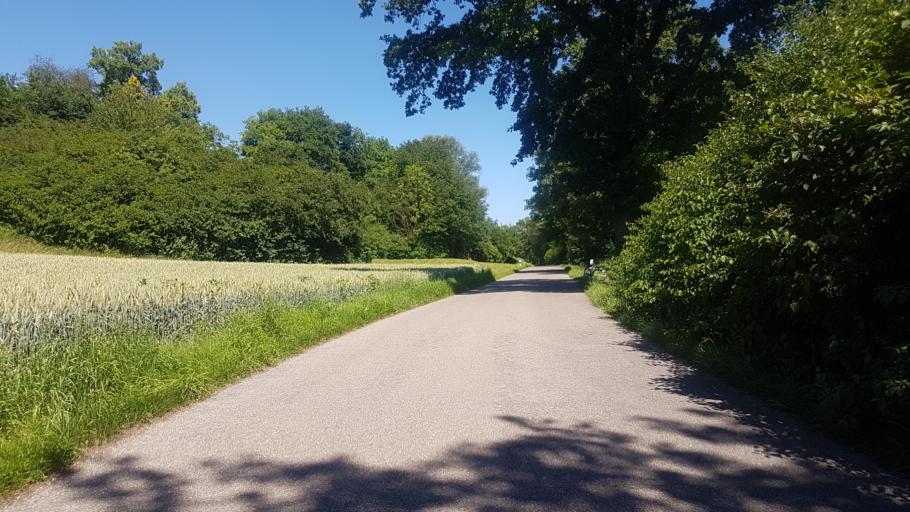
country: DE
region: Bavaria
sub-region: Upper Bavaria
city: Vohburg an der Donau
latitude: 48.7834
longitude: 11.6489
